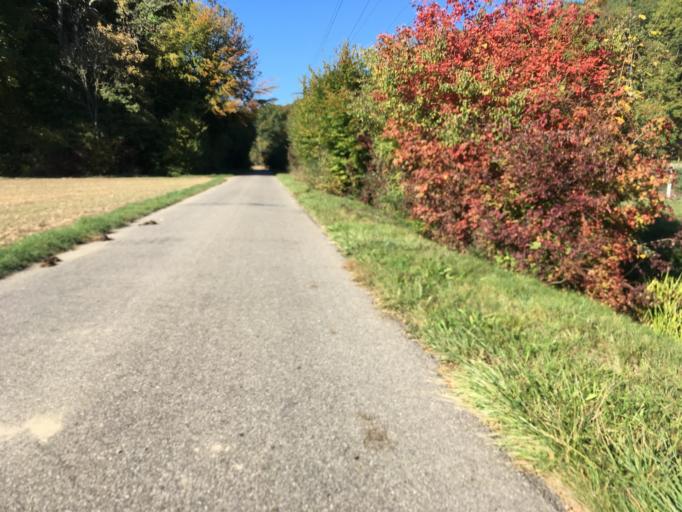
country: CH
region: Zurich
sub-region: Bezirk Buelach
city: Buelach / Soligaenter
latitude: 47.5366
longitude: 8.5438
